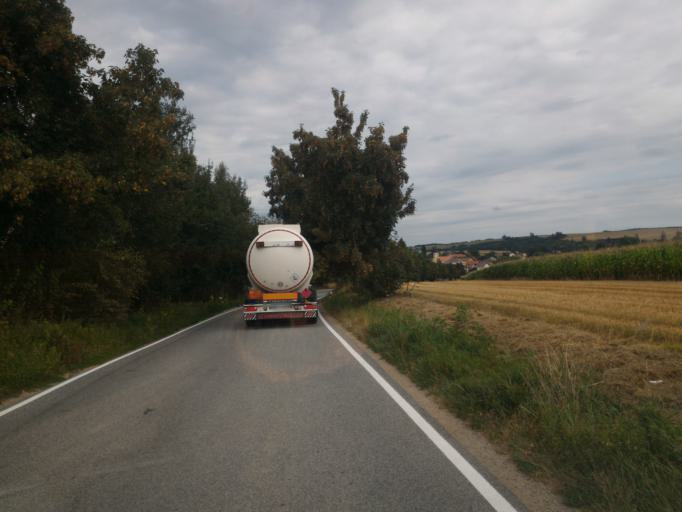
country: CZ
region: Vysocina
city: Zeletava
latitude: 49.1719
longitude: 15.5882
